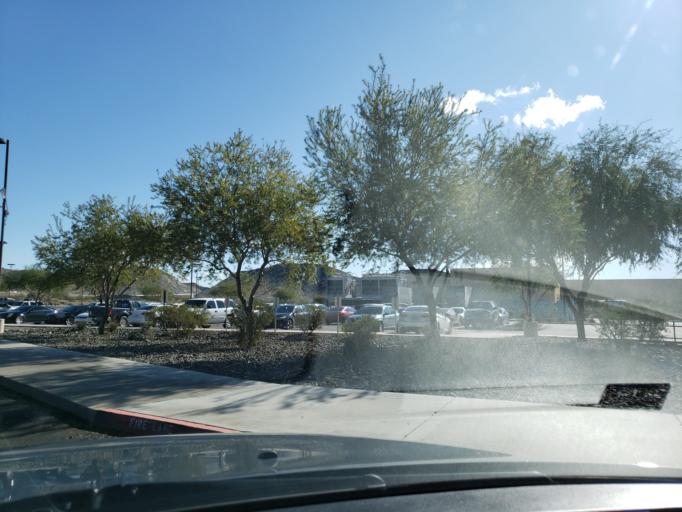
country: US
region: Arizona
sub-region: Maricopa County
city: Laveen
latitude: 33.3106
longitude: -112.1564
